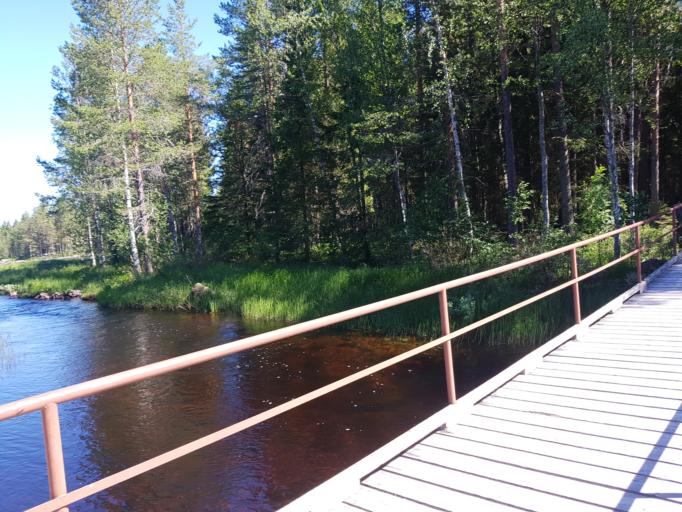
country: FI
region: Kainuu
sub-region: Kehys-Kainuu
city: Kuhmo
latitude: 64.1931
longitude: 29.5914
